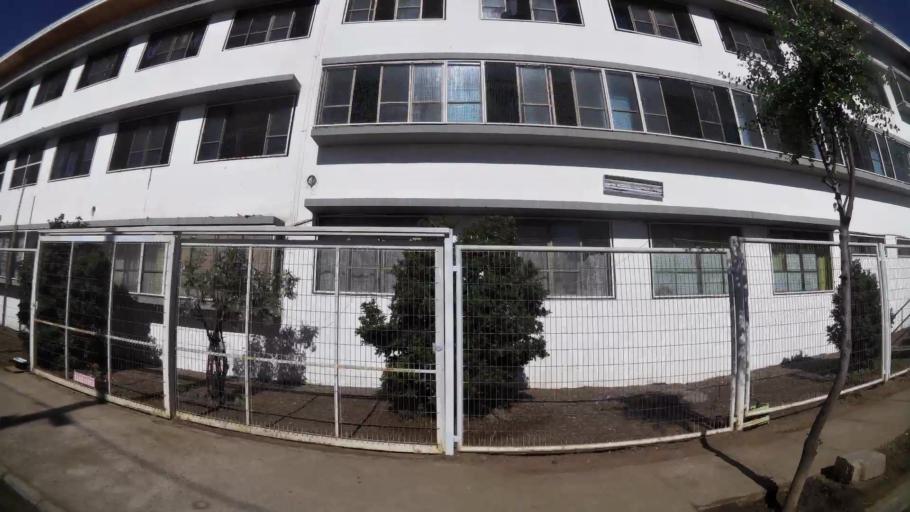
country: CL
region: Santiago Metropolitan
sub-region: Provincia de Chacabuco
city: Lampa
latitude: -33.3991
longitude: -71.1306
